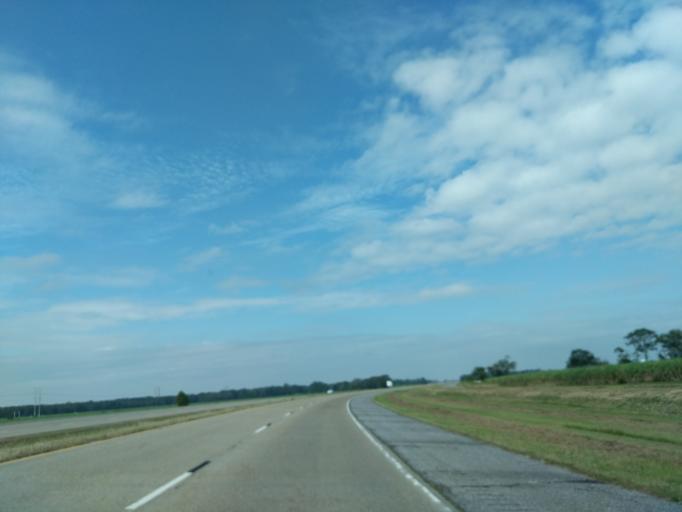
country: US
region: Louisiana
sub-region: Saint Mary Parish
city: Franklin
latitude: 29.7577
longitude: -91.4720
